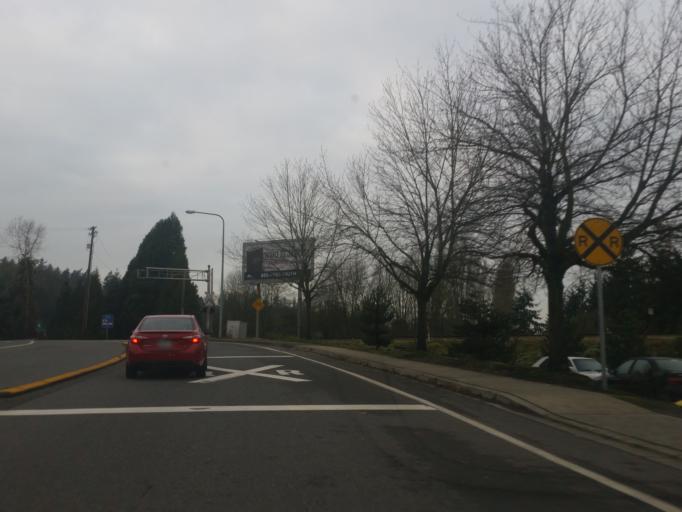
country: US
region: Washington
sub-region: King County
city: Woodinville
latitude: 47.7546
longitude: -122.1661
